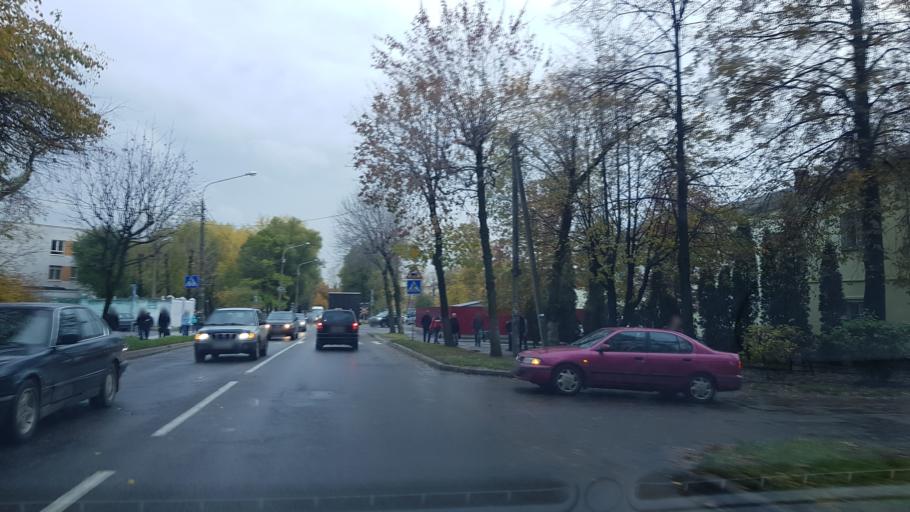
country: BY
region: Minsk
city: Syenitsa
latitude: 53.8454
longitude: 27.5470
